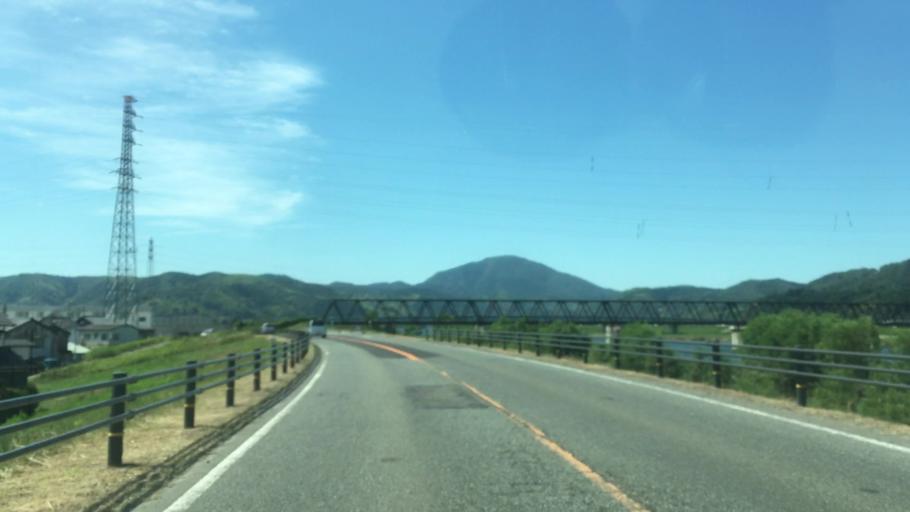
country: JP
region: Hyogo
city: Toyooka
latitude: 35.5510
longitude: 134.8241
